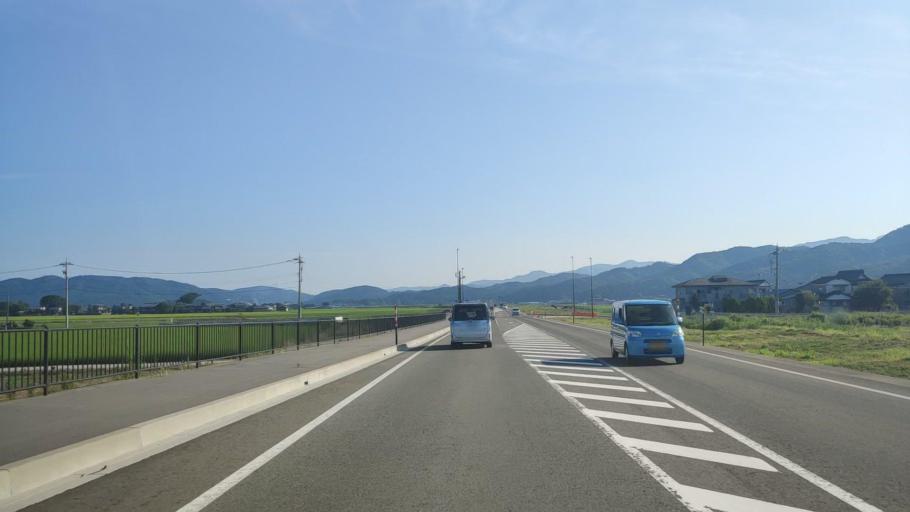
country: JP
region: Fukui
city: Maruoka
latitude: 36.1752
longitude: 136.2651
